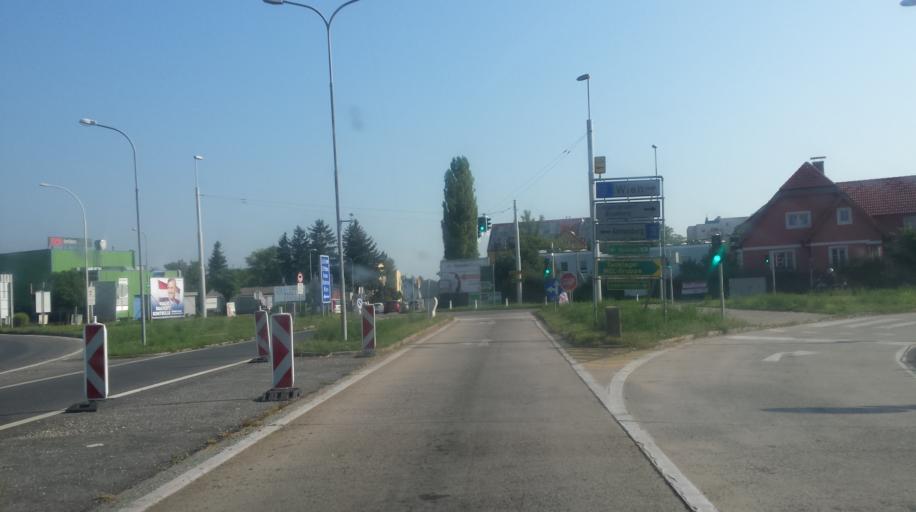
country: AT
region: Lower Austria
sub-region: Politischer Bezirk Korneuburg
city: Bisamberg
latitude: 48.3362
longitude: 16.3402
